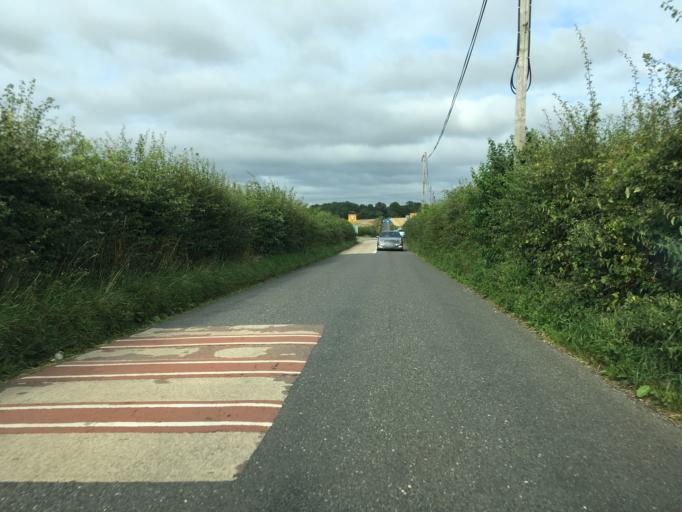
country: GB
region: England
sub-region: Hampshire
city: Colden Common
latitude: 51.0144
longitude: -1.2531
